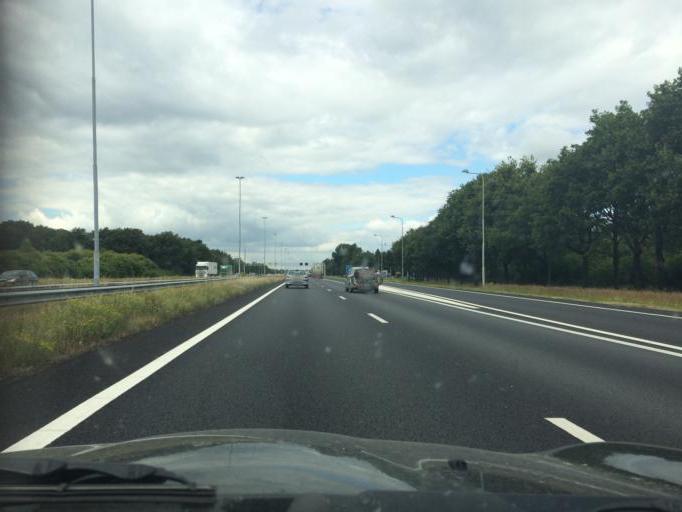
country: NL
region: North Brabant
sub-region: Gemeente Goirle
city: Goirle
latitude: 51.5389
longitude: 5.0134
